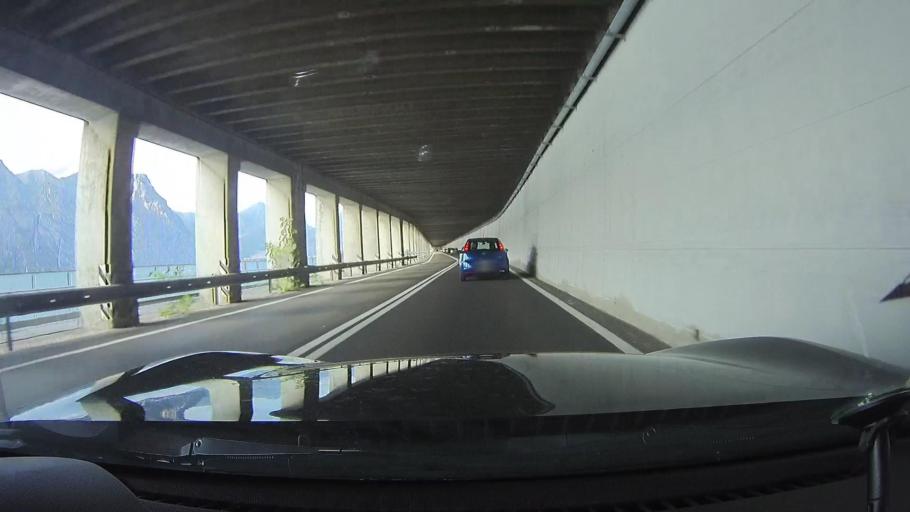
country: IT
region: Trentino-Alto Adige
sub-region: Provincia di Trento
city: Torbole sul Garda
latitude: 45.8201
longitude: 10.8552
